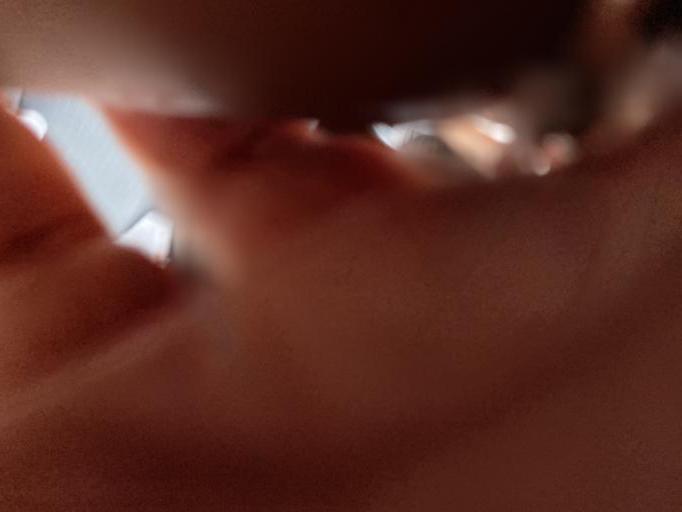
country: US
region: Florida
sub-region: Lake County
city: Four Corners
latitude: 28.3971
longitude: -81.6913
